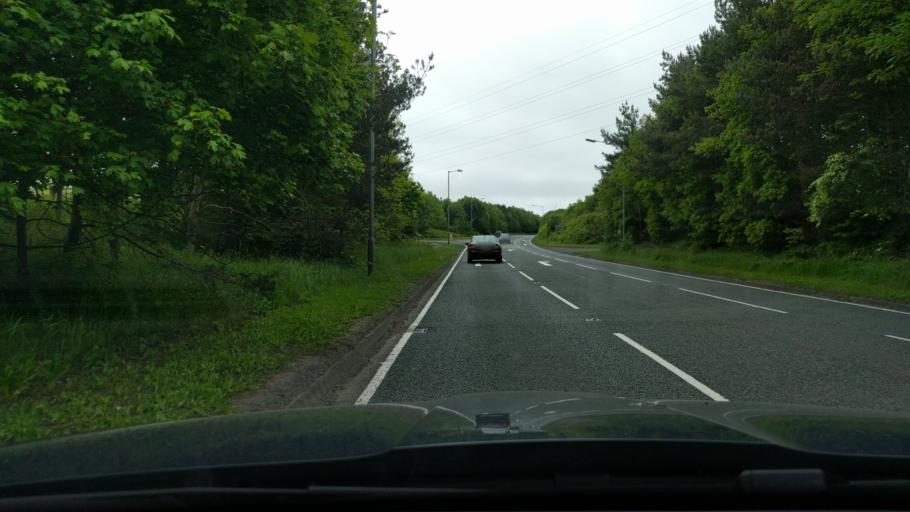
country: GB
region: England
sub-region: Northumberland
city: Cresswell
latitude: 55.2170
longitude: -1.5711
